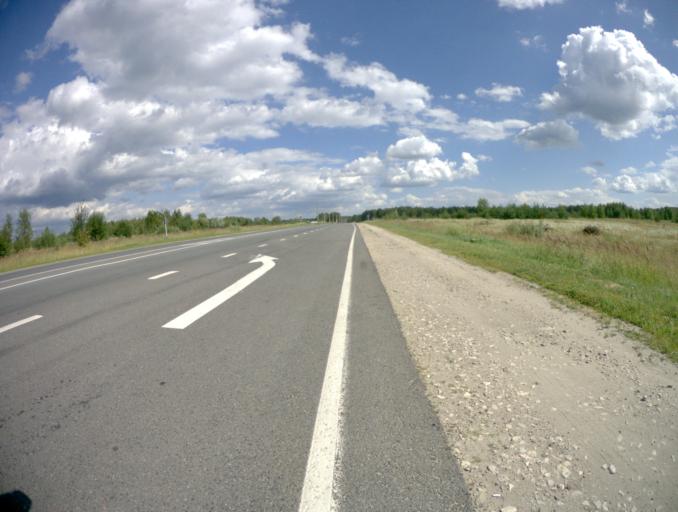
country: RU
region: Vladimir
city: Andreyevo
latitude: 55.9370
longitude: 41.0719
